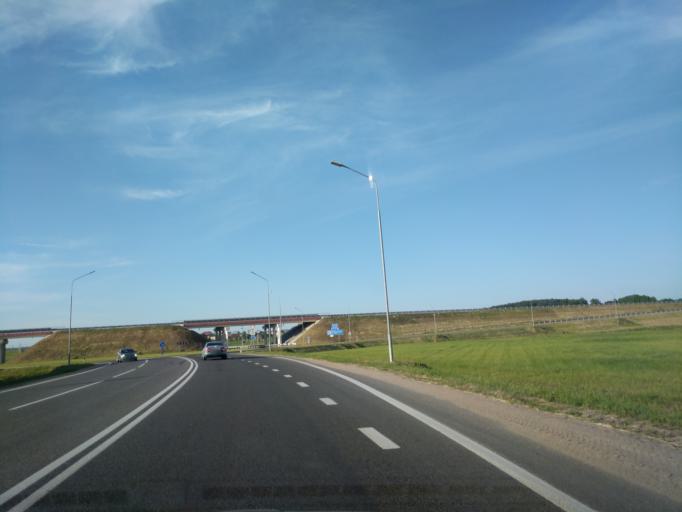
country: BY
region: Grodnenskaya
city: Ashmyany
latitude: 54.4343
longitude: 25.9655
